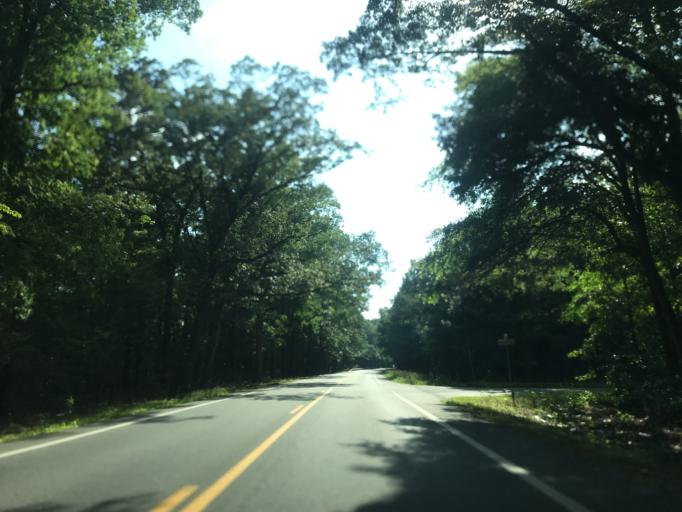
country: US
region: Maryland
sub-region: Wicomico County
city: Hebron
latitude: 38.4641
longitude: -75.7281
